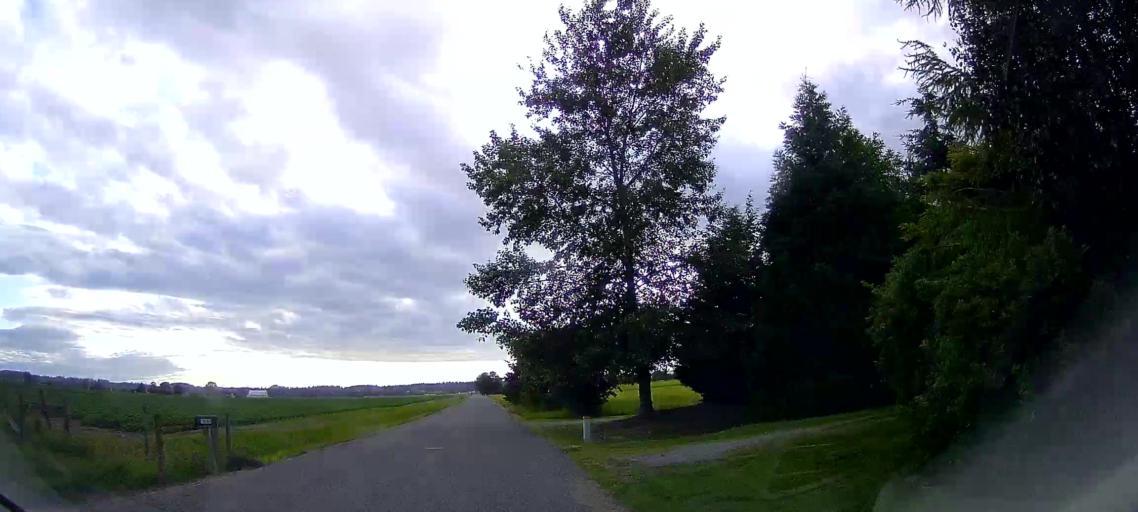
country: US
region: Washington
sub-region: Skagit County
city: Mount Vernon
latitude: 48.3848
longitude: -122.3878
